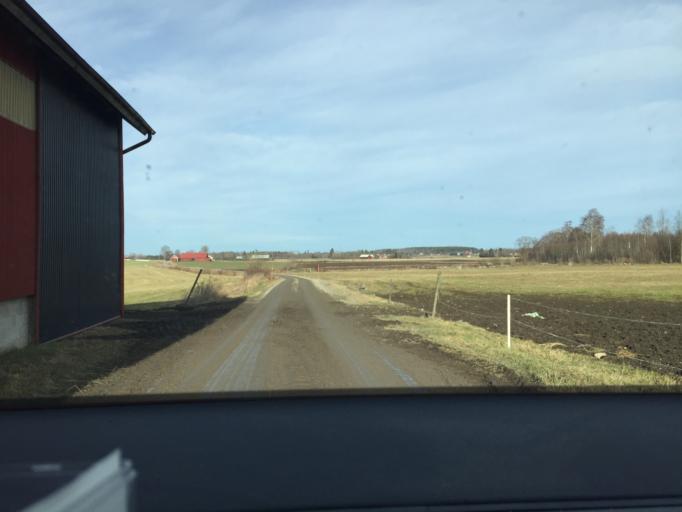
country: SE
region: OErebro
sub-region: Hallsbergs Kommun
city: Skollersta
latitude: 59.1261
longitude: 15.4317
